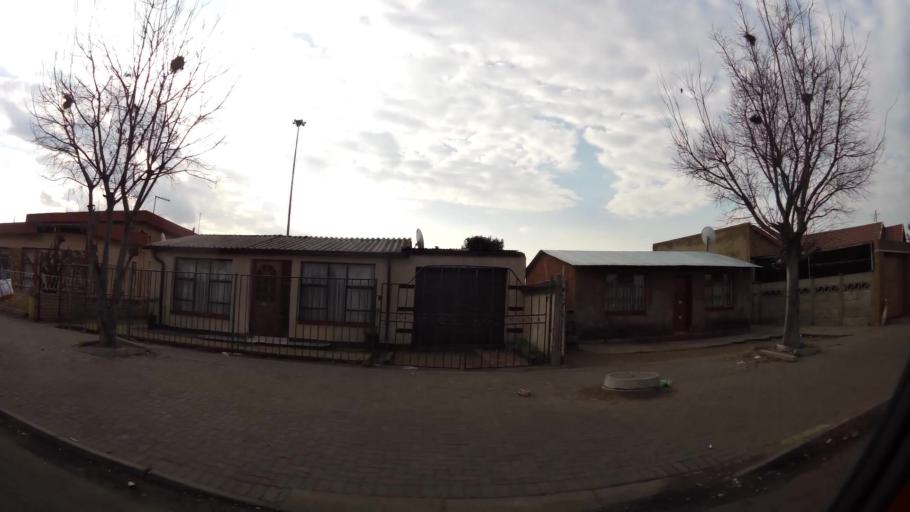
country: ZA
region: Gauteng
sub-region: Sedibeng District Municipality
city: Vanderbijlpark
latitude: -26.6965
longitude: 27.8753
